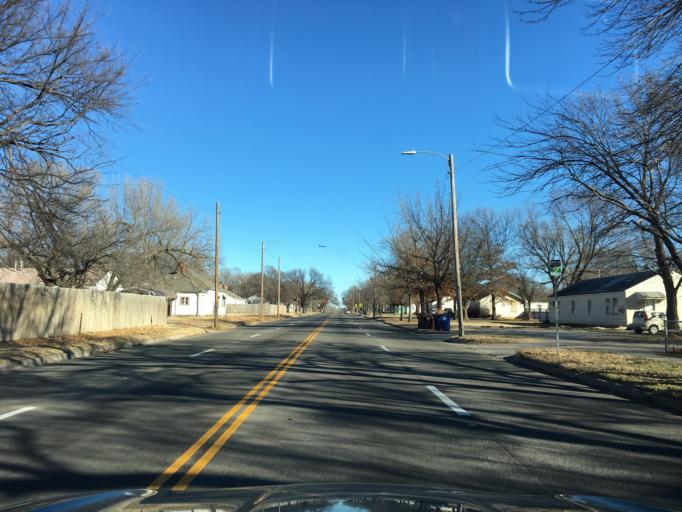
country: US
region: Kansas
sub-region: Sedgwick County
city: Wichita
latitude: 37.6719
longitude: -97.2863
